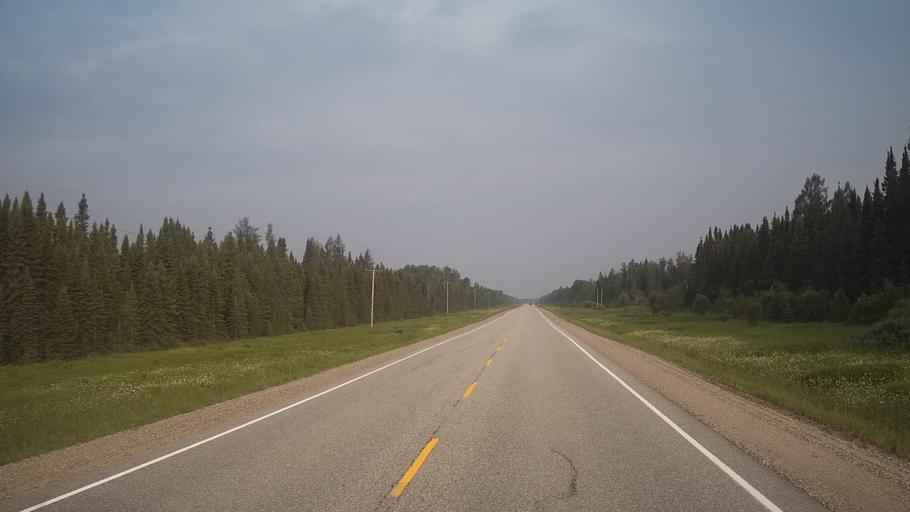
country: CA
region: Ontario
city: Hearst
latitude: 49.7323
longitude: -83.9200
